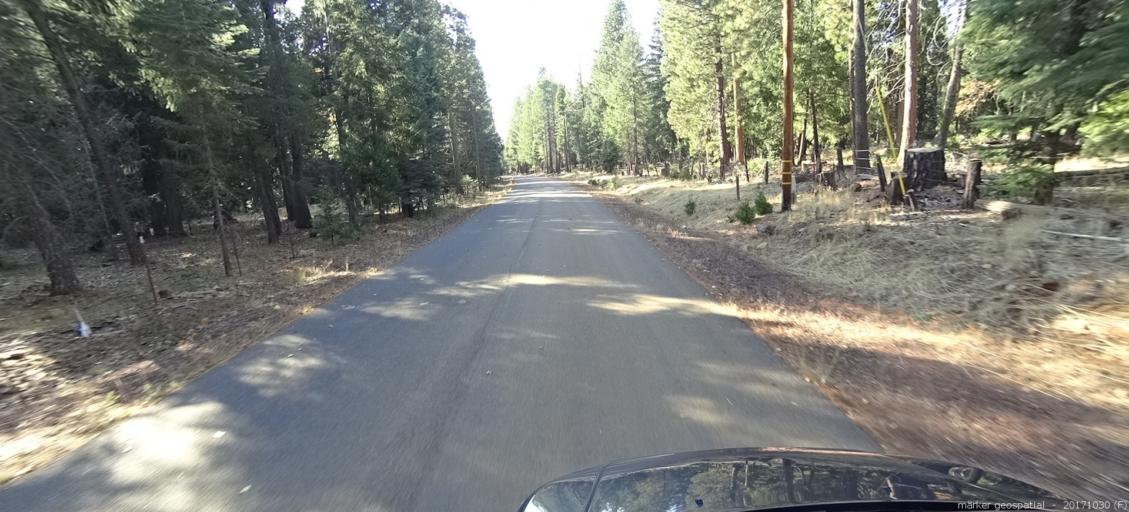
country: US
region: California
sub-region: Shasta County
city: Shingletown
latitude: 40.5341
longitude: -121.7184
